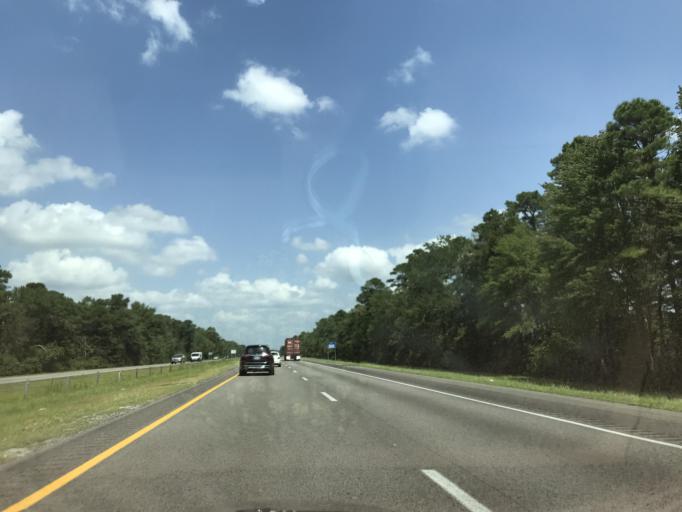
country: US
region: North Carolina
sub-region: Pender County
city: Rocky Point
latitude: 34.3970
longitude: -77.8735
